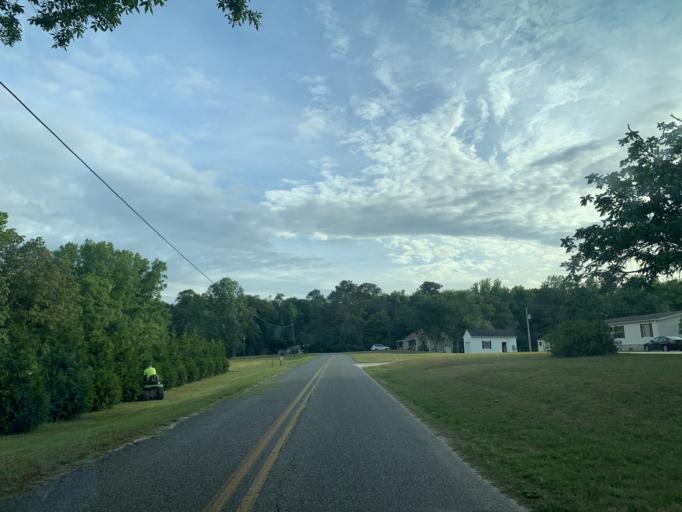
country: US
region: Maryland
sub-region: Worcester County
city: Pocomoke City
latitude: 38.0804
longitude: -75.4764
